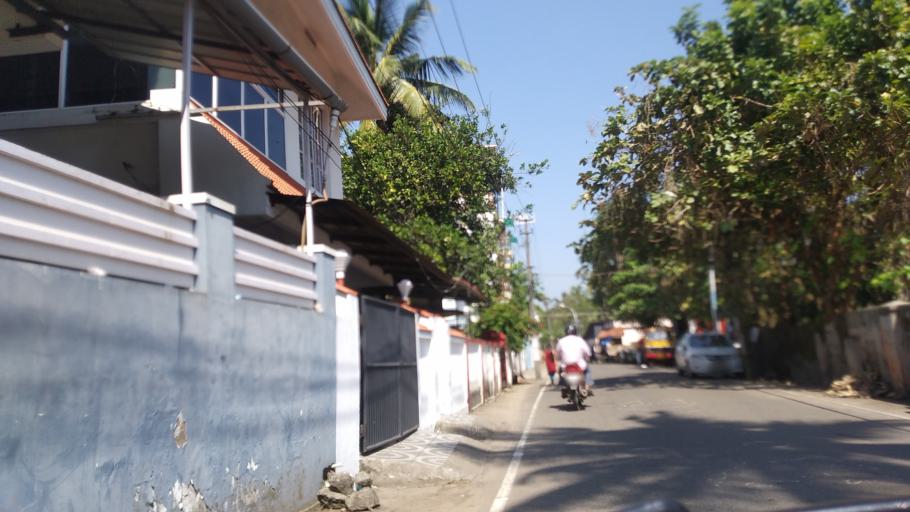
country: IN
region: Kerala
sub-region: Ernakulam
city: Cochin
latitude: 9.9387
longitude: 76.2485
